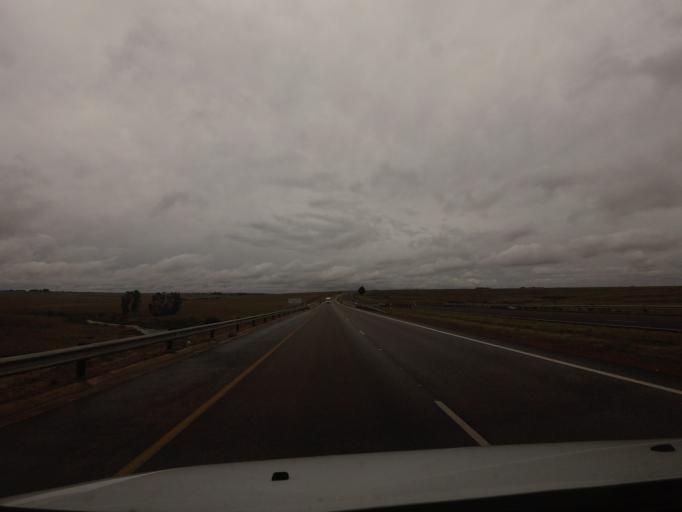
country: ZA
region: Mpumalanga
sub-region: Nkangala District Municipality
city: Middelburg
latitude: -25.8175
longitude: 29.5896
